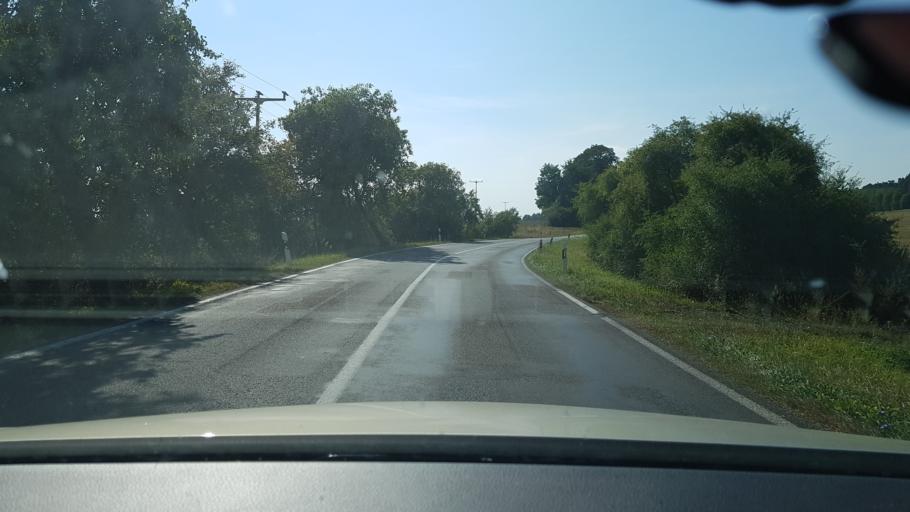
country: DE
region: Brandenburg
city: Lawitz
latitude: 52.1156
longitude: 14.5895
